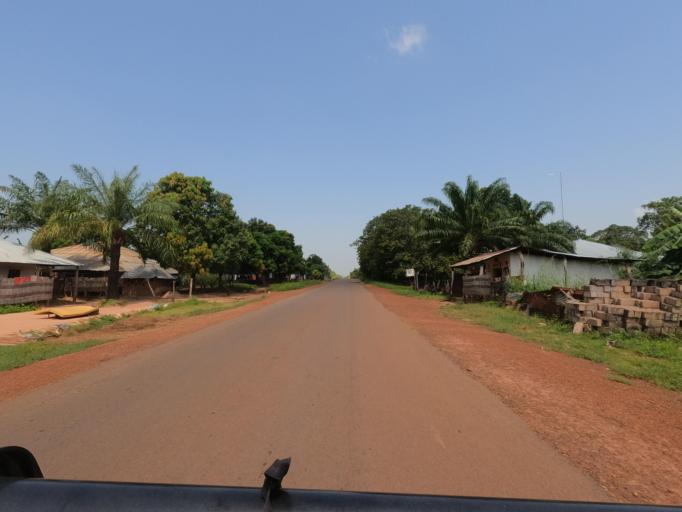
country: SN
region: Ziguinchor
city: Adeane
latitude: 12.3721
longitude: -15.7767
